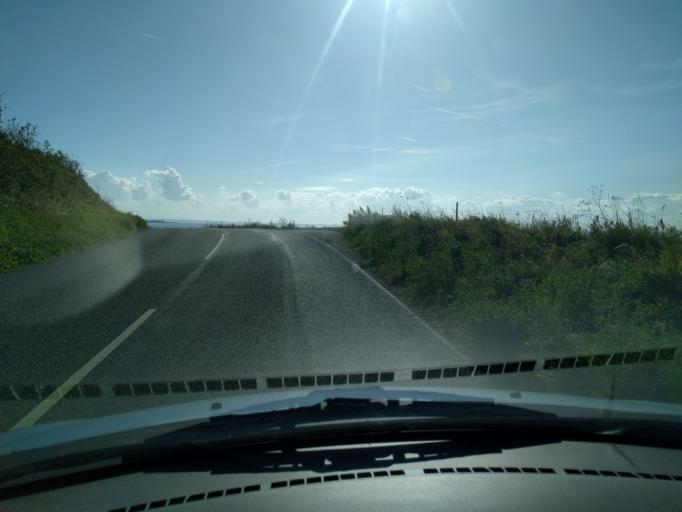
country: DK
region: South Denmark
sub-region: Assens Kommune
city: Assens
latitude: 55.1723
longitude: 9.9851
